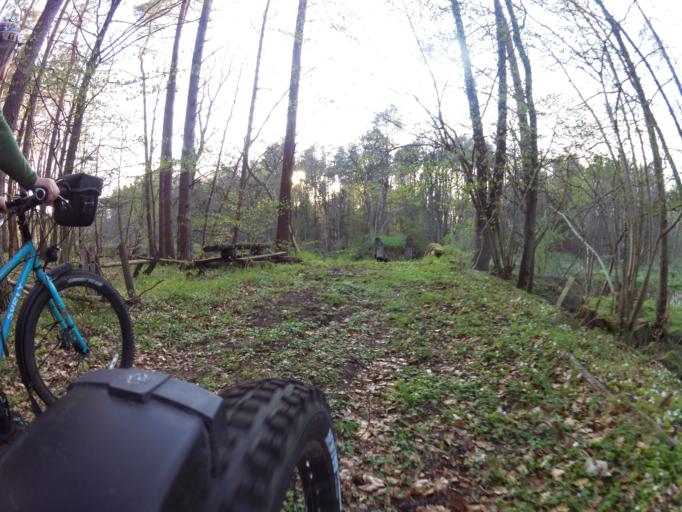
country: PL
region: West Pomeranian Voivodeship
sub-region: Powiat gryficki
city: Ploty
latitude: 53.7538
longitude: 15.3033
